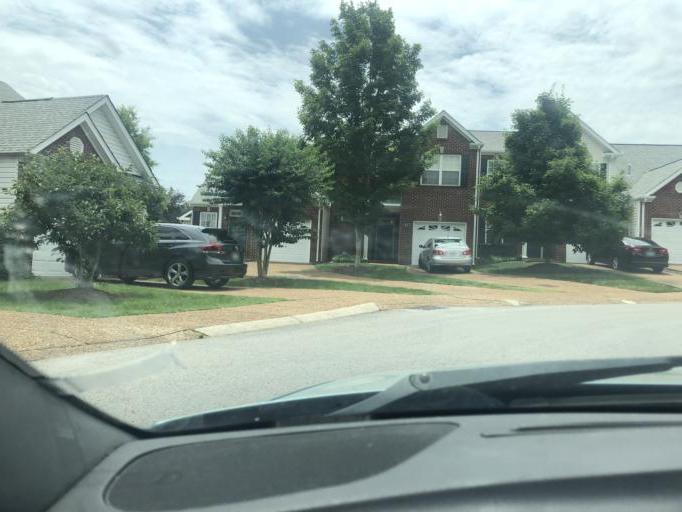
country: US
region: Tennessee
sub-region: Rutherford County
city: La Vergne
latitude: 36.1217
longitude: -86.6292
